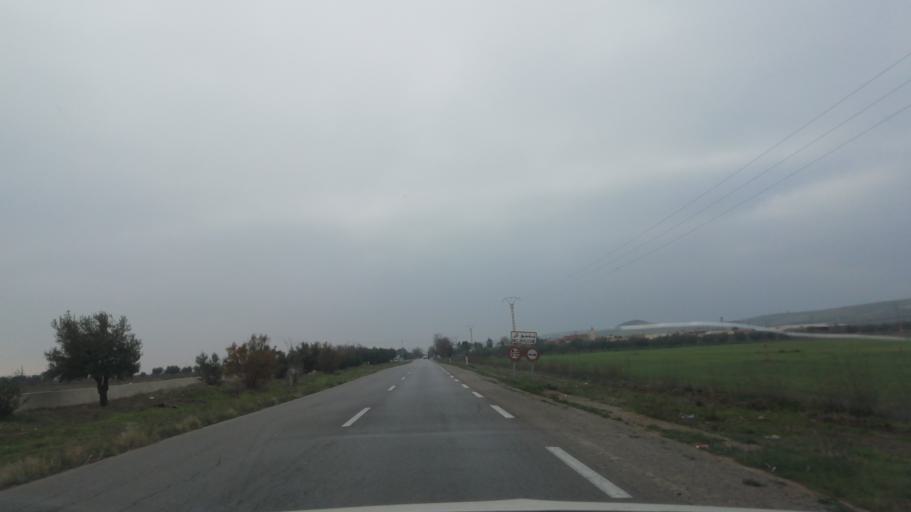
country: DZ
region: Sidi Bel Abbes
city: Sfizef
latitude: 35.2196
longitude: -0.2967
